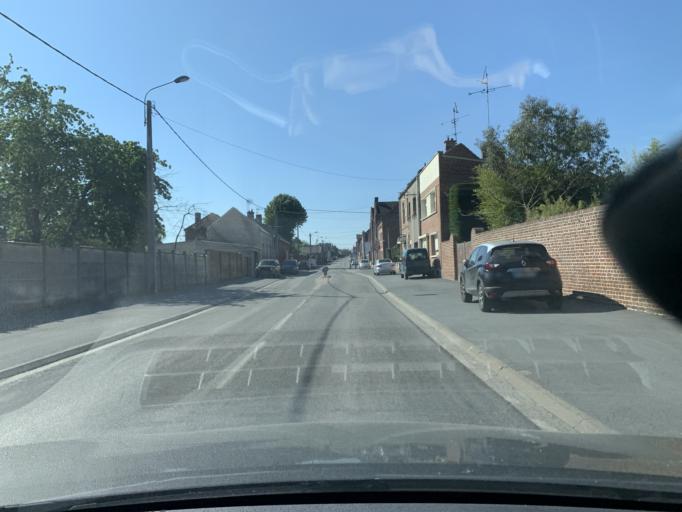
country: FR
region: Nord-Pas-de-Calais
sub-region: Departement du Nord
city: Cambrai
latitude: 50.1616
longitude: 3.2412
